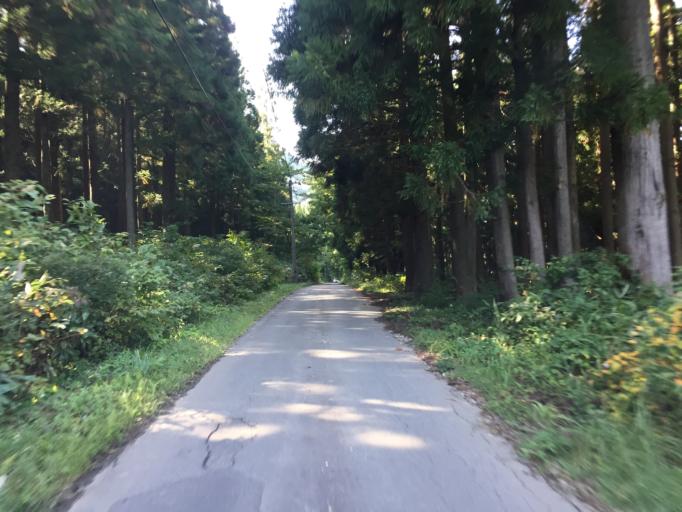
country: JP
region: Yamagata
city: Yonezawa
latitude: 37.8328
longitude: 140.2068
